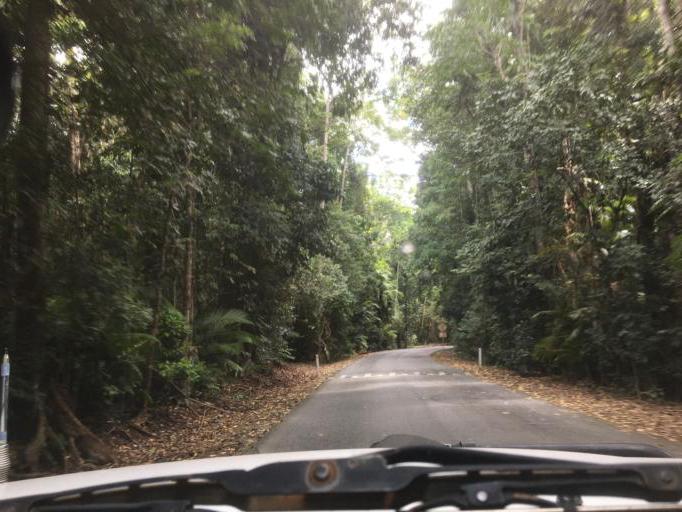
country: AU
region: Queensland
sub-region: Tablelands
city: Tolga
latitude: -17.2830
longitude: 145.6188
